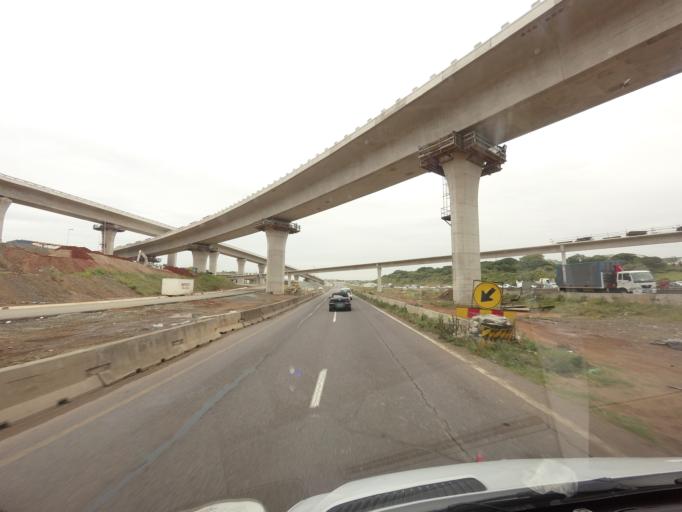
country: ZA
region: KwaZulu-Natal
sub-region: eThekwini Metropolitan Municipality
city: Durban
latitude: -29.7236
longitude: 31.0586
